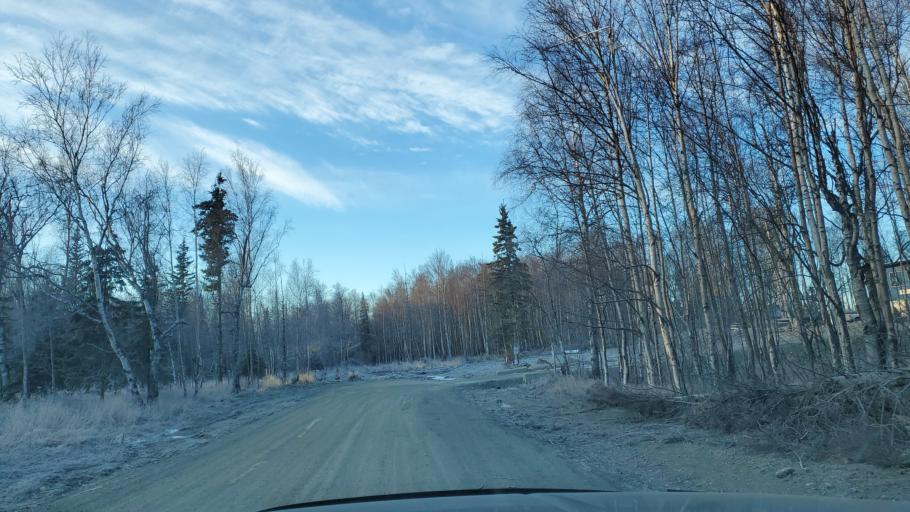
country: US
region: Alaska
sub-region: Matanuska-Susitna Borough
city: Wasilla
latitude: 61.5767
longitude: -149.4227
